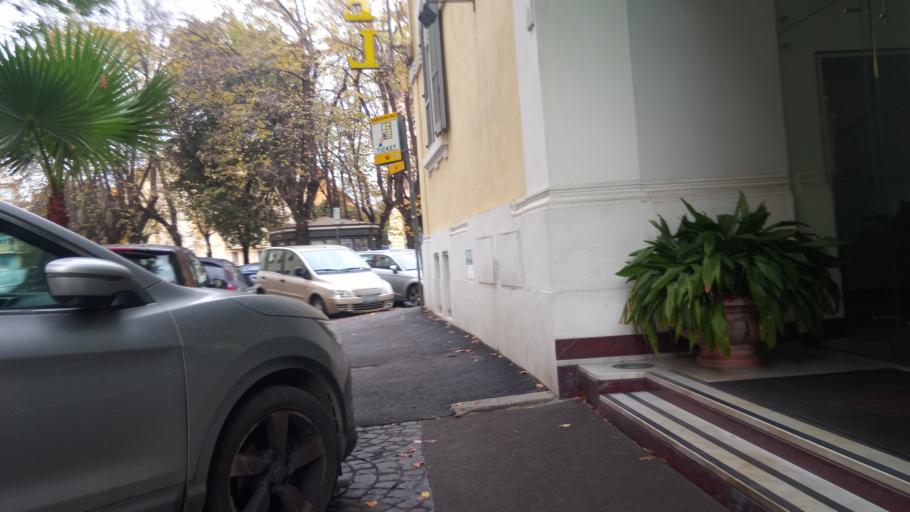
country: IT
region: Latium
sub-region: Citta metropolitana di Roma Capitale
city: Rome
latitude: 41.8985
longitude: 12.5116
